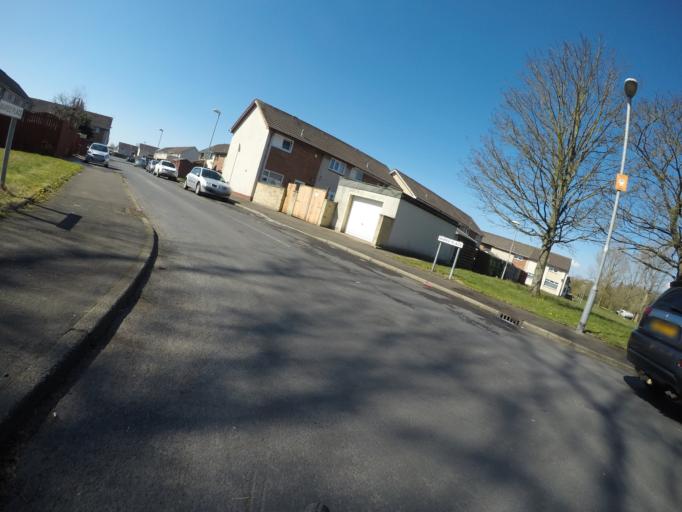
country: GB
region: Scotland
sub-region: North Ayrshire
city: Irvine
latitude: 55.6344
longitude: -4.6606
